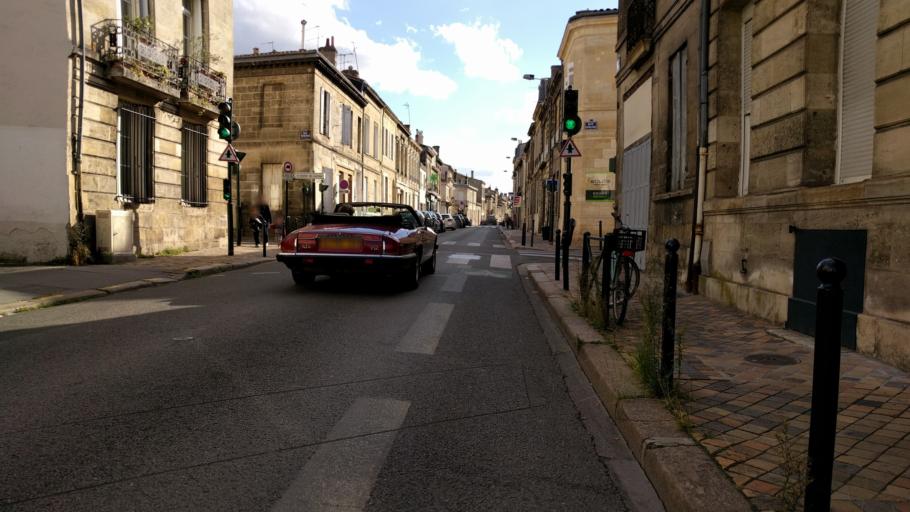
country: FR
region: Aquitaine
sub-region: Departement de la Gironde
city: Bordeaux
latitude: 44.8472
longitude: -0.5878
